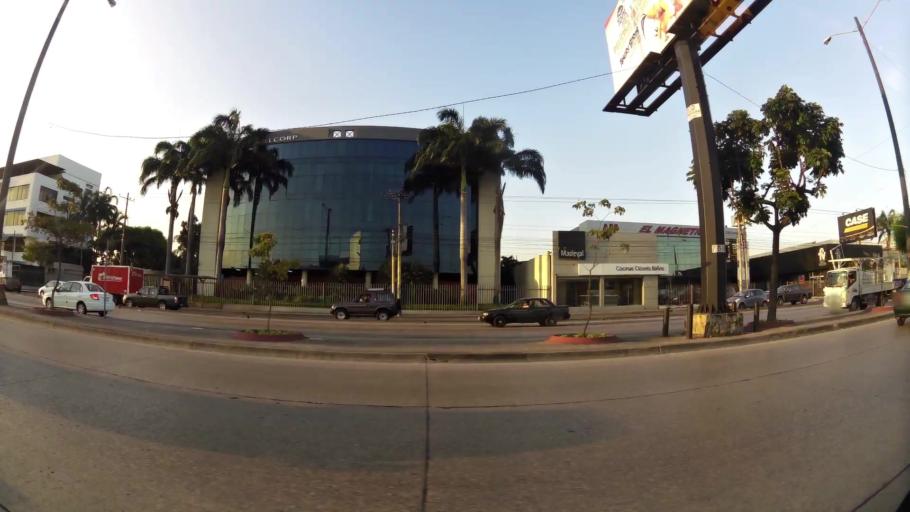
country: EC
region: Guayas
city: Eloy Alfaro
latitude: -2.1501
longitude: -79.9003
